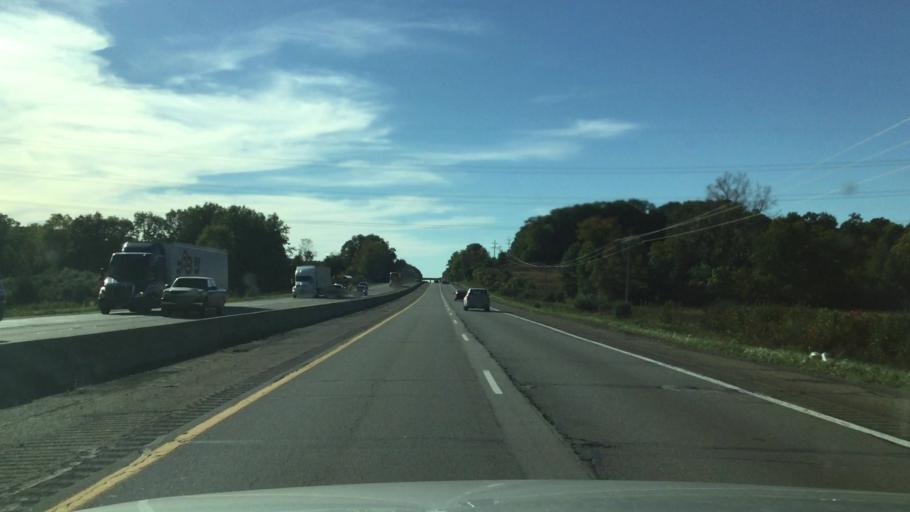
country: US
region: Michigan
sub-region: Jackson County
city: Spring Arbor
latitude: 42.2691
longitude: -84.5064
